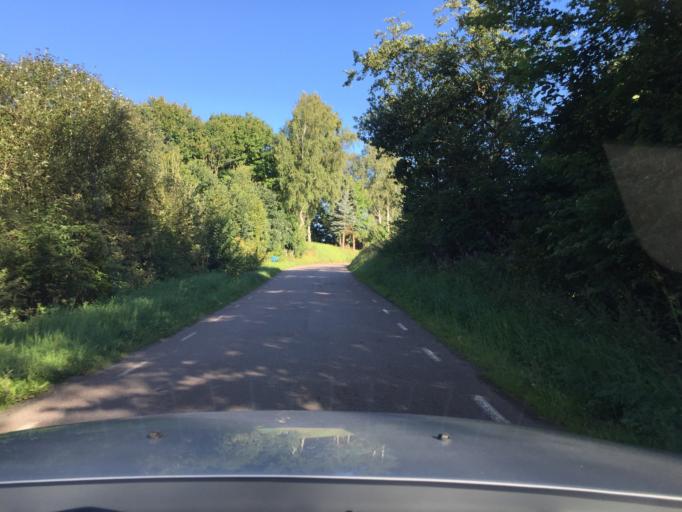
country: SE
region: Skane
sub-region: Hassleholms Kommun
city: Sosdala
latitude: 56.0383
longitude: 13.7331
